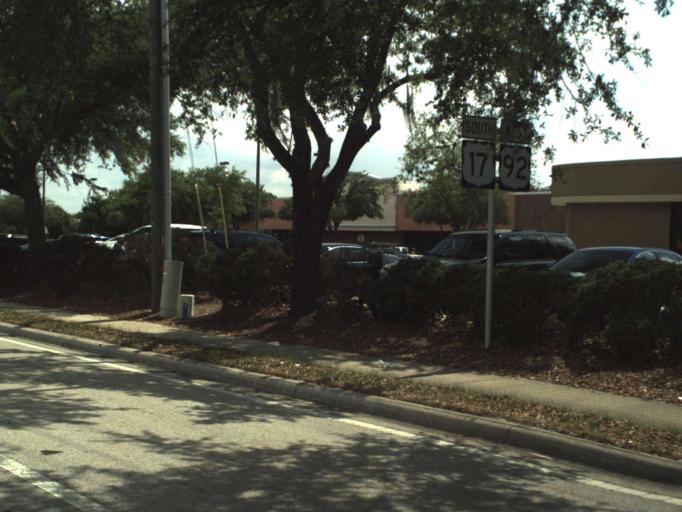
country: US
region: Florida
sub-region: Seminole County
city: Longwood
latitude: 28.6973
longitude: -81.3274
